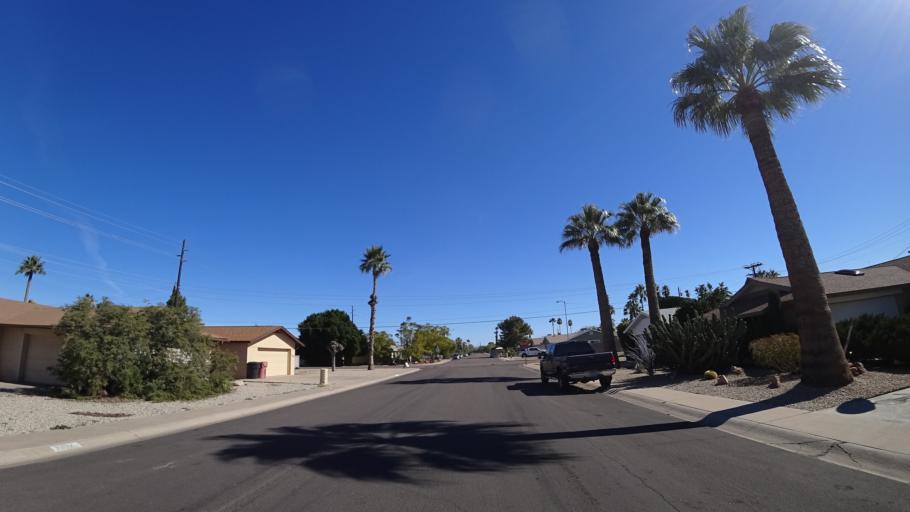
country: US
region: Arizona
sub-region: Maricopa County
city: Scottsdale
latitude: 33.5130
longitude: -111.8966
